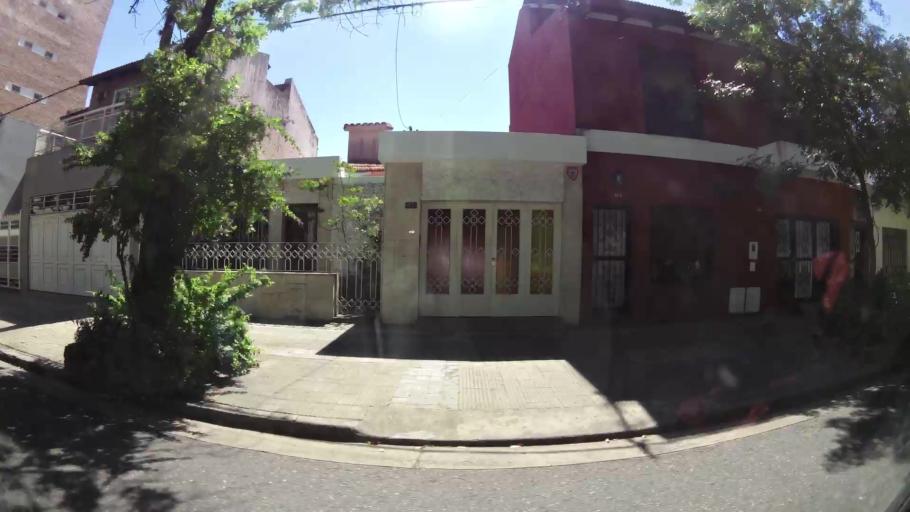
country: AR
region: Santa Fe
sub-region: Departamento de Rosario
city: Rosario
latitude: -32.9370
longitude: -60.6744
